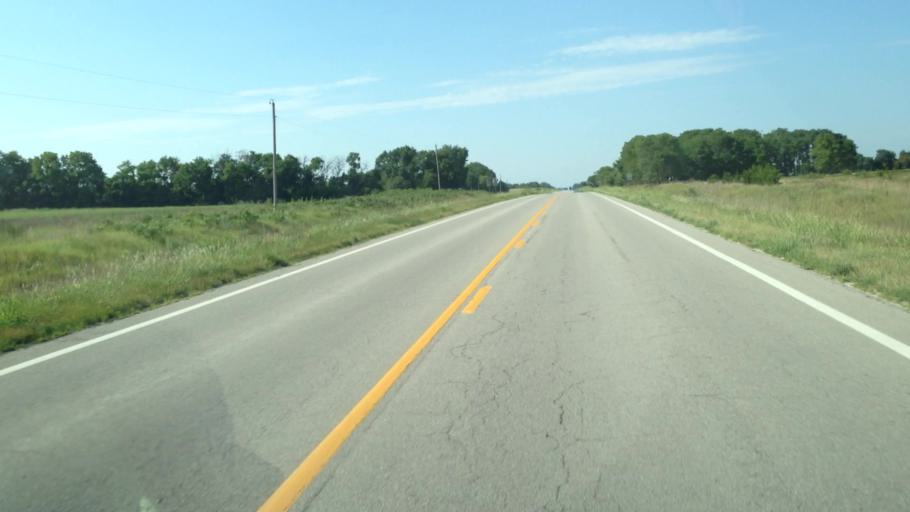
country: US
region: Kansas
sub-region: Neosho County
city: Erie
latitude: 37.7207
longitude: -95.1607
